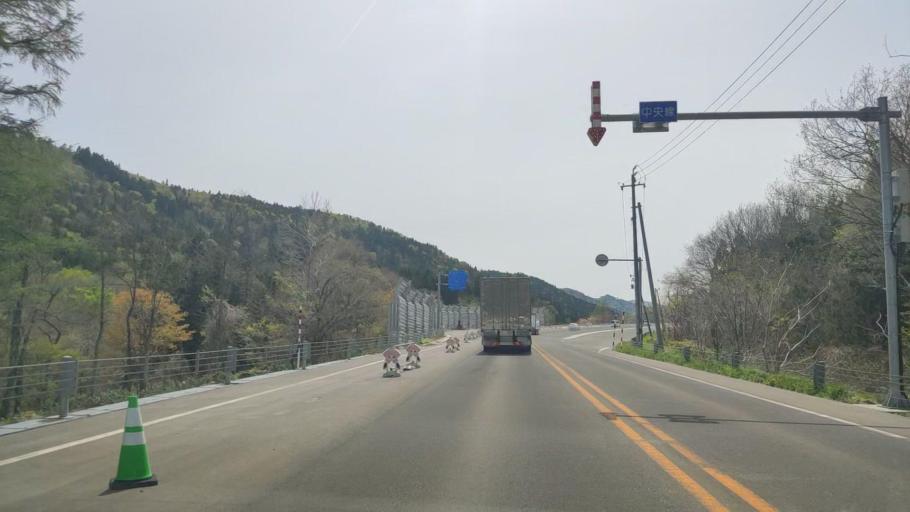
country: JP
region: Aomori
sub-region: Misawa Shi
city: Inuotose
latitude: 40.7848
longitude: 141.0687
